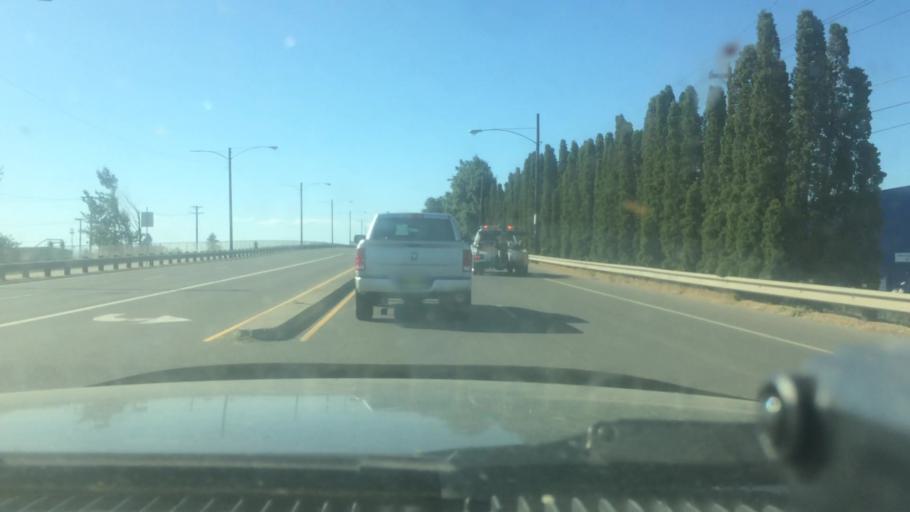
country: US
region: Oregon
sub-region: Lane County
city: Eugene
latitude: 44.0578
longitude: -123.1312
